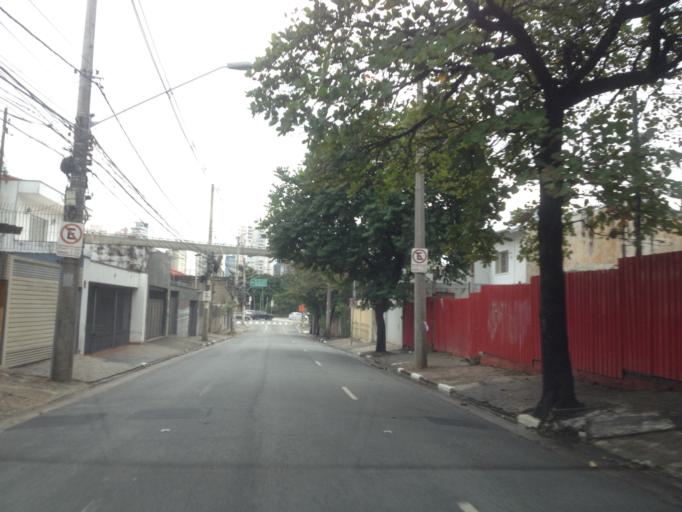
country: BR
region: Sao Paulo
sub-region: Sao Paulo
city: Sao Paulo
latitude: -23.6135
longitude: -46.6914
